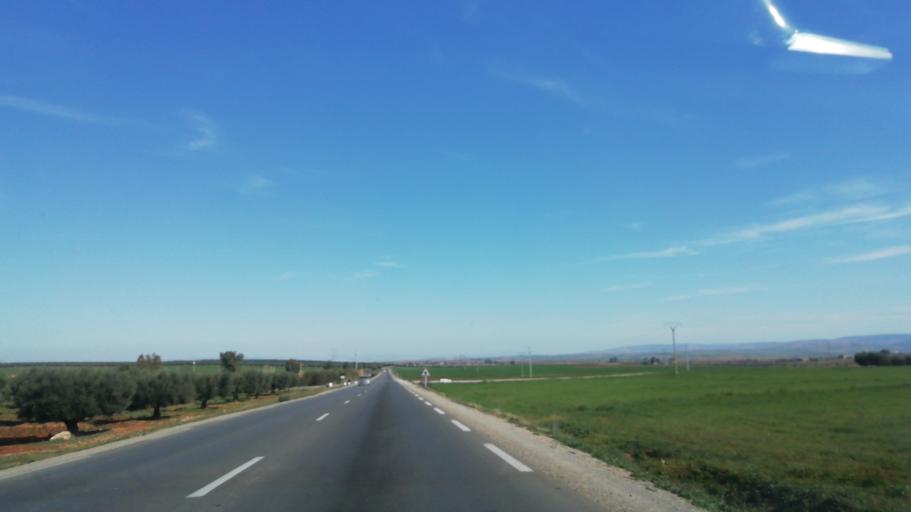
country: DZ
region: Mascara
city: Mascara
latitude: 35.4178
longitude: 0.4110
